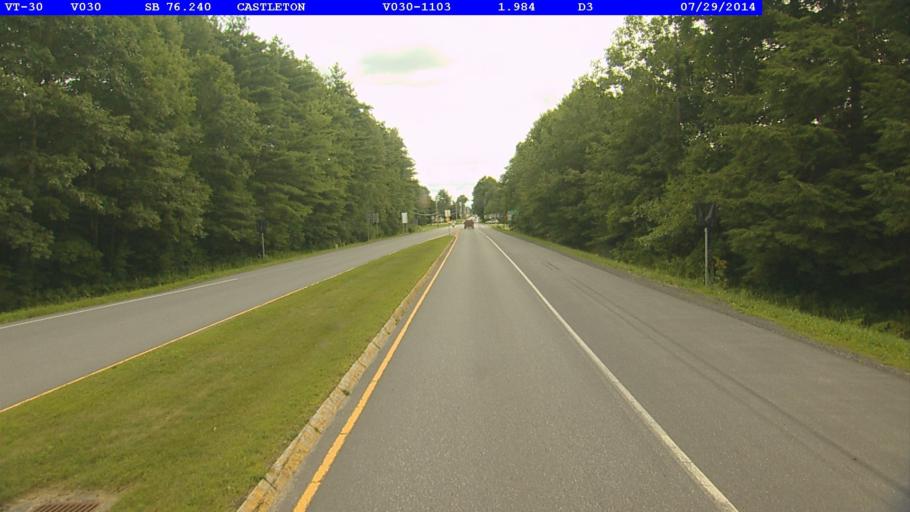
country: US
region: Vermont
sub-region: Rutland County
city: Castleton
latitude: 43.6151
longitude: -73.2070
